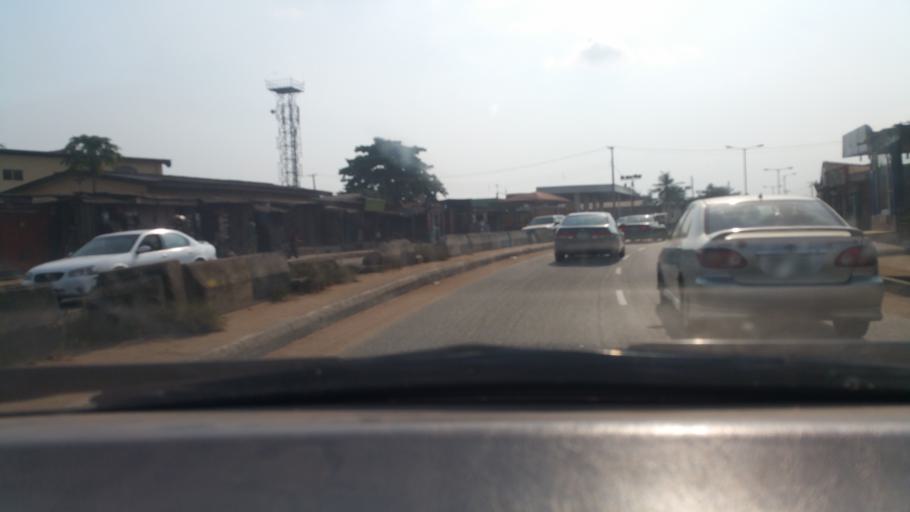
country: NG
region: Lagos
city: Ikotun
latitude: 6.5779
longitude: 3.2831
